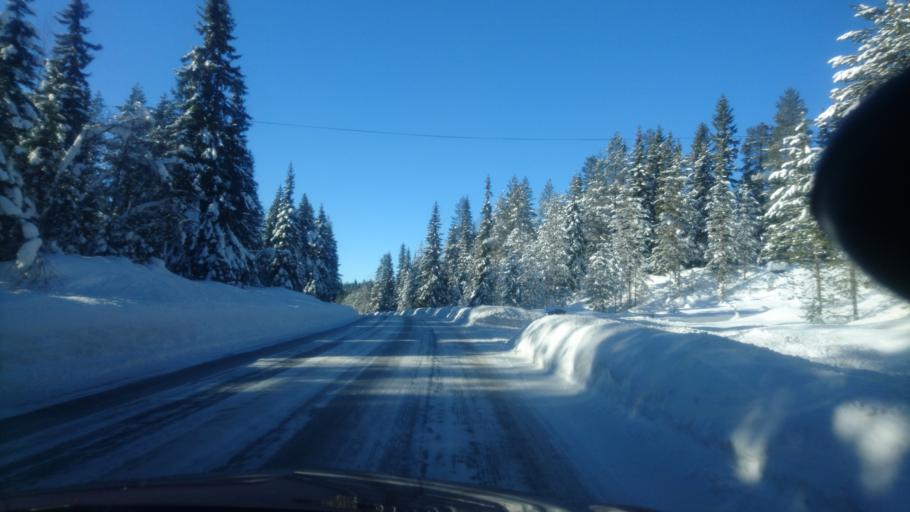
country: NO
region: Hedmark
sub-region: Trysil
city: Innbygda
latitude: 61.2719
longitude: 12.4690
